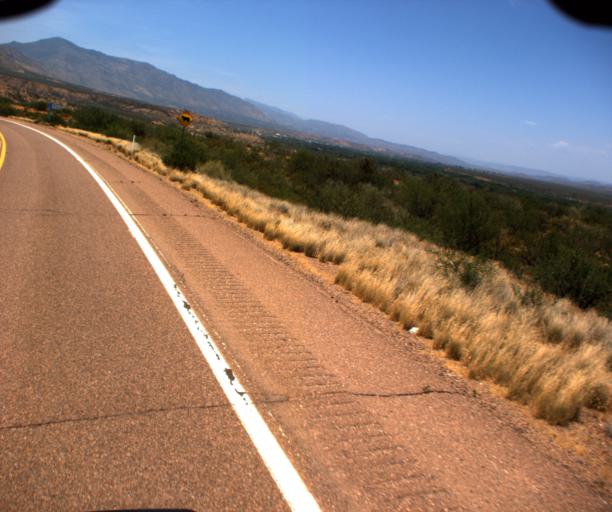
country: US
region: Arizona
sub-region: Gila County
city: Tonto Basin
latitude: 33.8082
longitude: -111.2831
